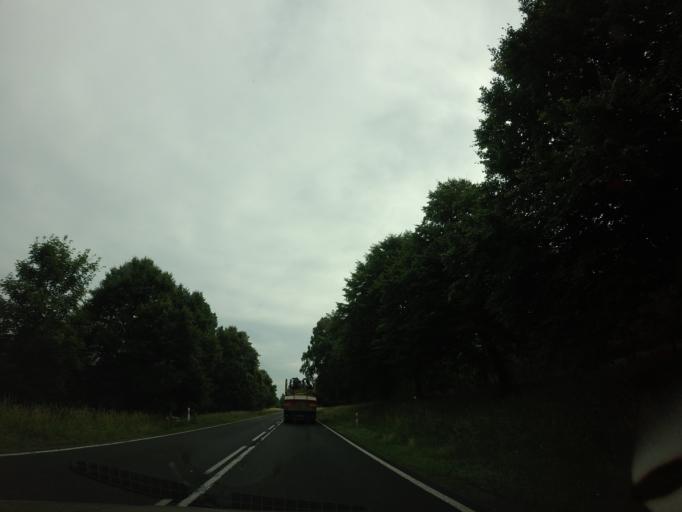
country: PL
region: West Pomeranian Voivodeship
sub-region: Powiat drawski
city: Kalisz Pomorski
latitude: 53.2973
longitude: 15.9646
